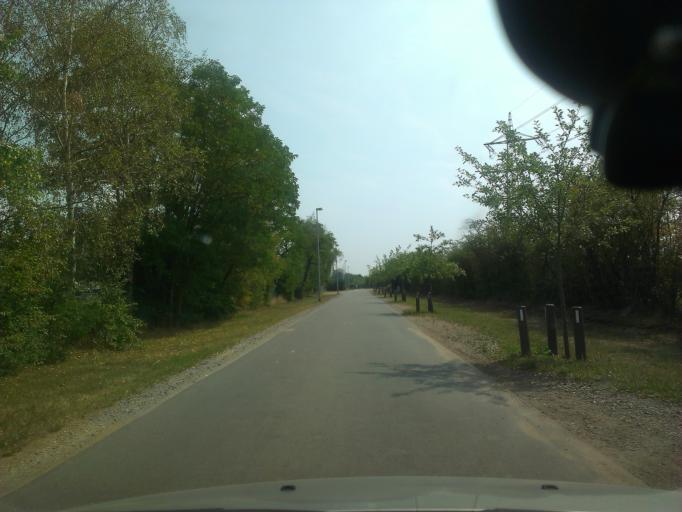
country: DE
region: Hesse
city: Viernheim
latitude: 49.5458
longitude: 8.5551
